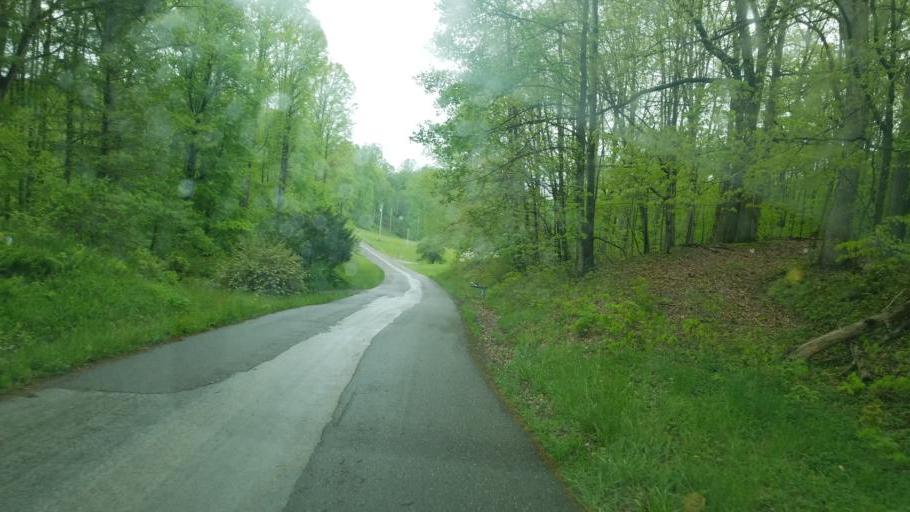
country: US
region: Ohio
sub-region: Tuscarawas County
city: Rockford
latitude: 40.3969
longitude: -81.1645
